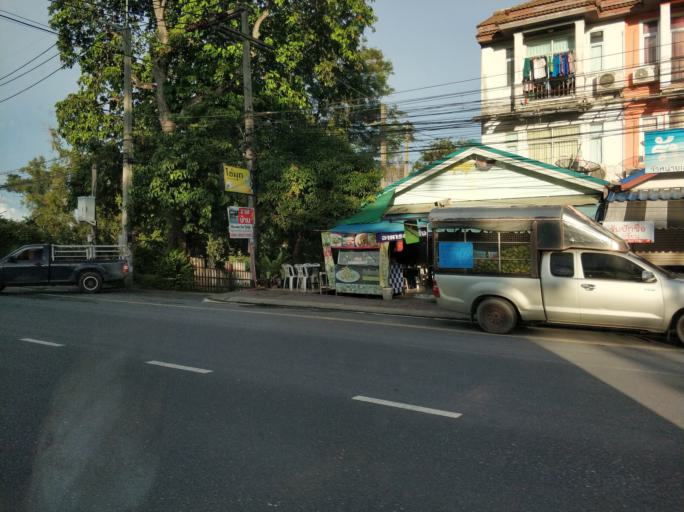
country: TH
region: Phuket
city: Kathu
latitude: 7.9067
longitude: 98.3363
